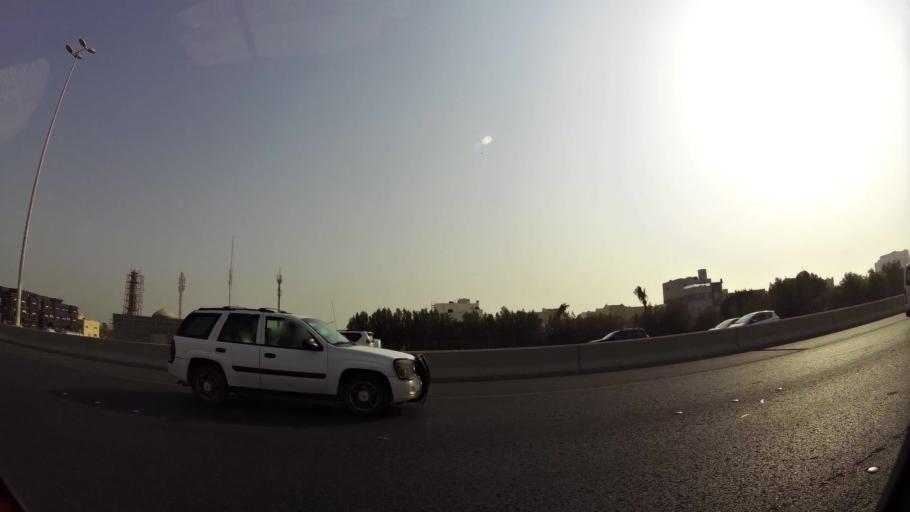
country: KW
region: Al Ahmadi
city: Al Fintas
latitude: 29.1886
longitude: 48.1105
